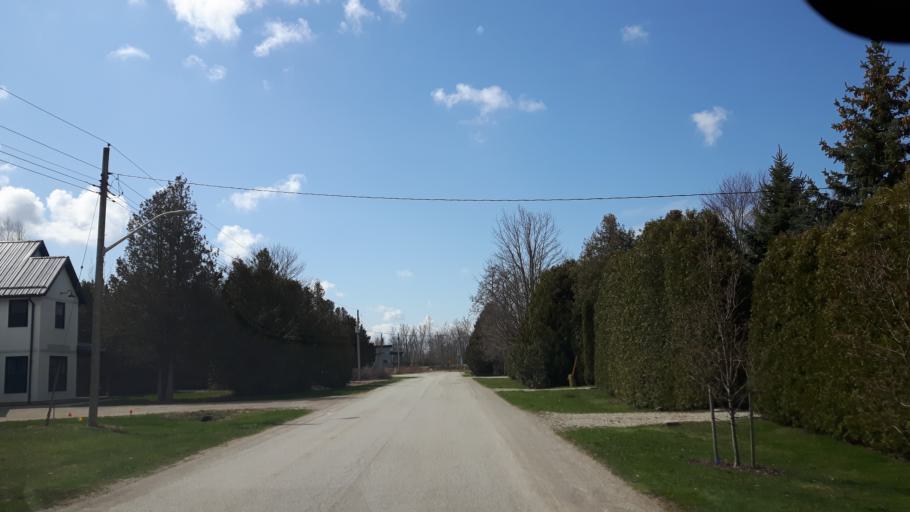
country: CA
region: Ontario
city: Bluewater
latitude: 43.5528
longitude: -81.7050
